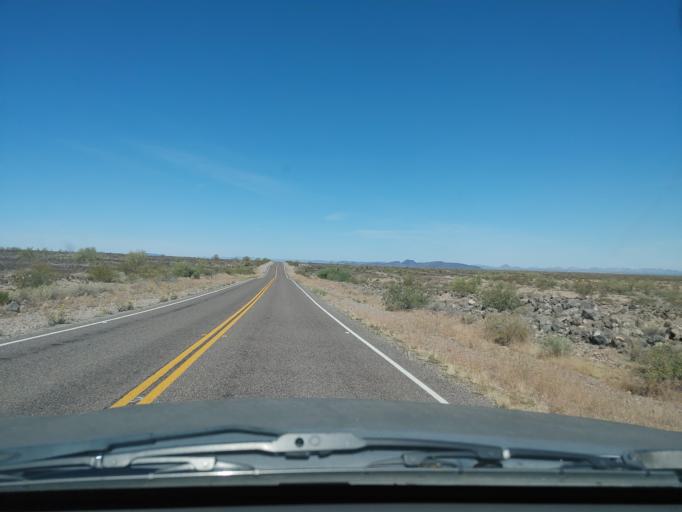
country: US
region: Arizona
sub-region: Maricopa County
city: Gila Bend
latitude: 32.8937
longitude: -113.2456
